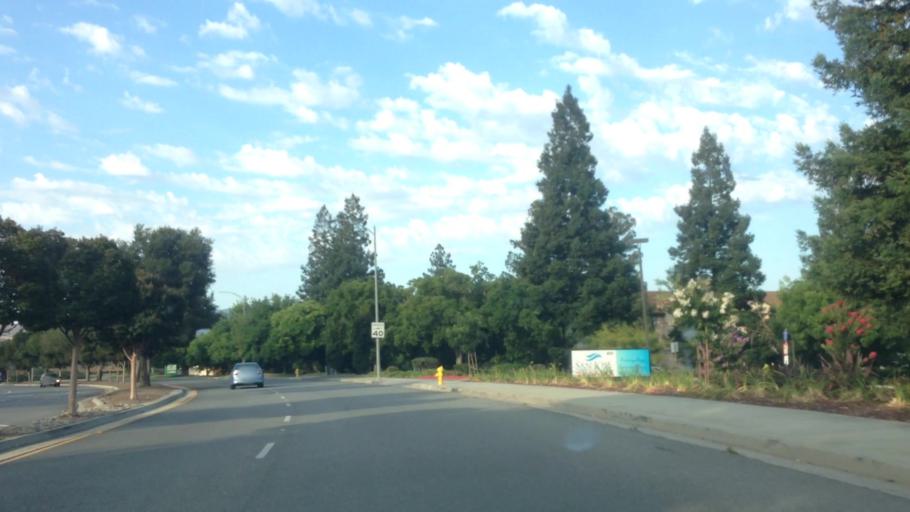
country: US
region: California
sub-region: Santa Clara County
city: Seven Trees
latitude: 37.2485
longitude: -121.7724
